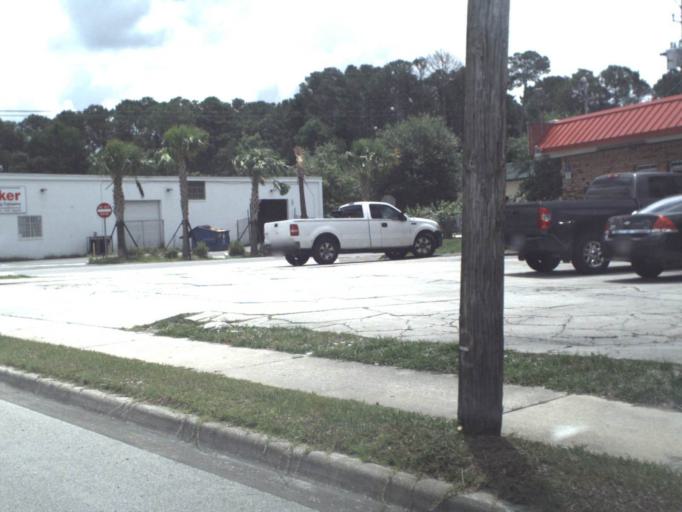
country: US
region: Florida
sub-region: Duval County
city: Jacksonville
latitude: 30.2850
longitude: -81.6389
